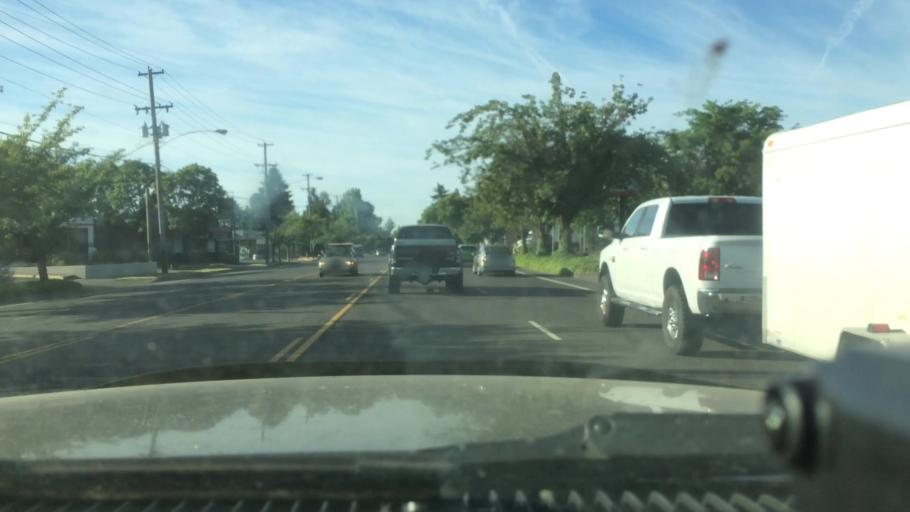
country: US
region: Oregon
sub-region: Lane County
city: Eugene
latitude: 44.0945
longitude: -123.1277
